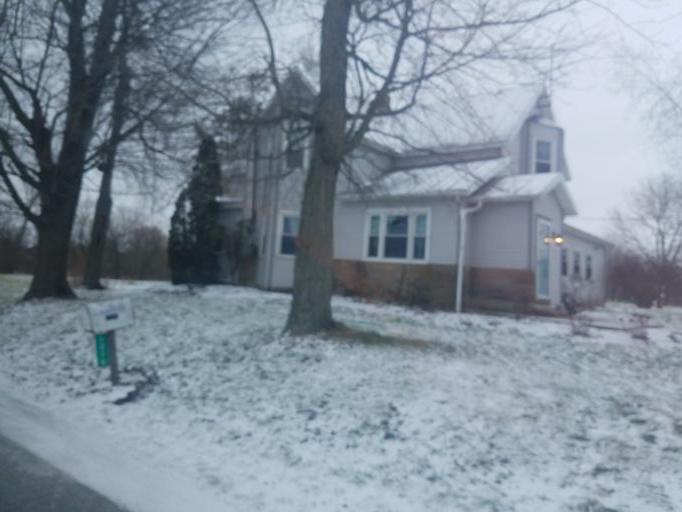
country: US
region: Ohio
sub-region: Delaware County
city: Sunbury
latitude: 40.2166
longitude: -82.7700
